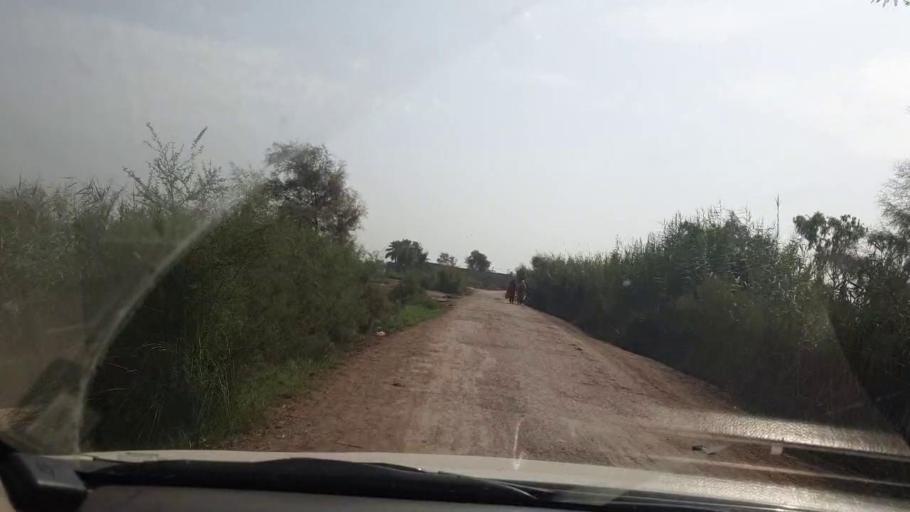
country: PK
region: Sindh
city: Lakhi
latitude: 27.8315
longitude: 68.7591
